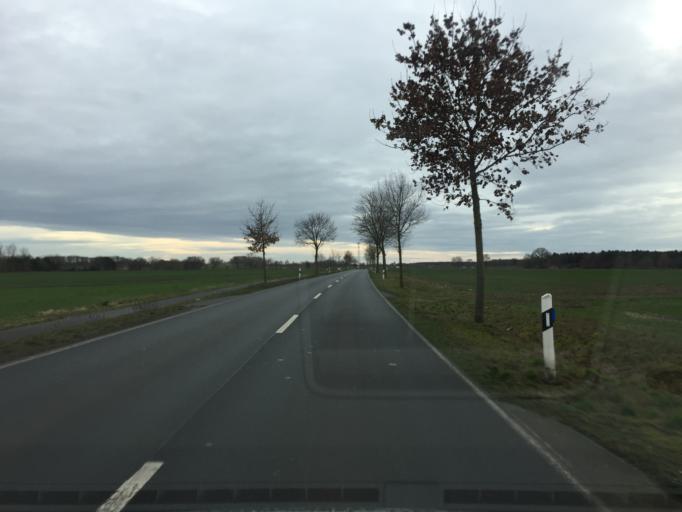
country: DE
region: Lower Saxony
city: Langwedel
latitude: 53.0131
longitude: 9.1705
